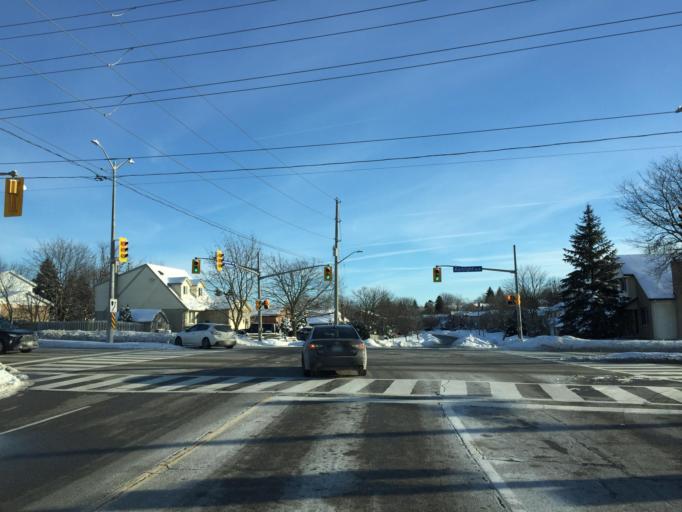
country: CA
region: Ontario
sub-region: Wellington County
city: Guelph
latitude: 43.5106
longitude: -80.2284
